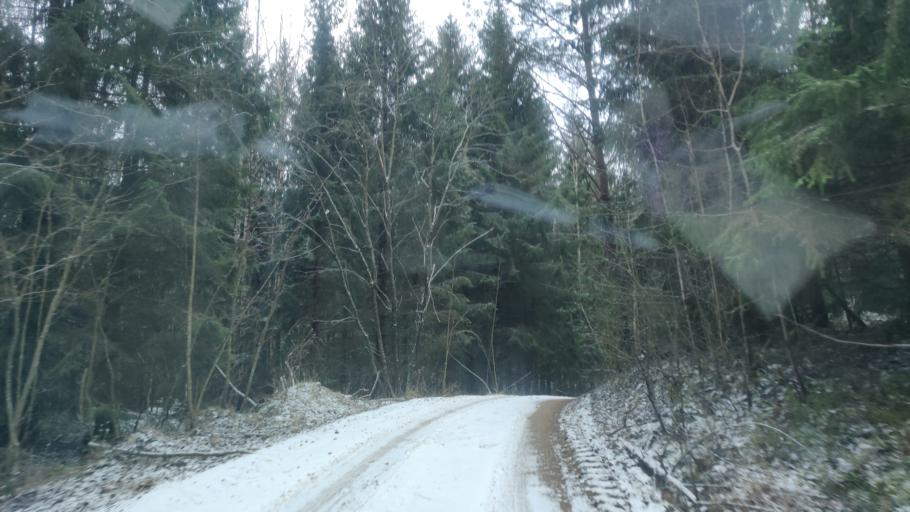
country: LT
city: Trakai
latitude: 54.5715
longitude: 24.9386
